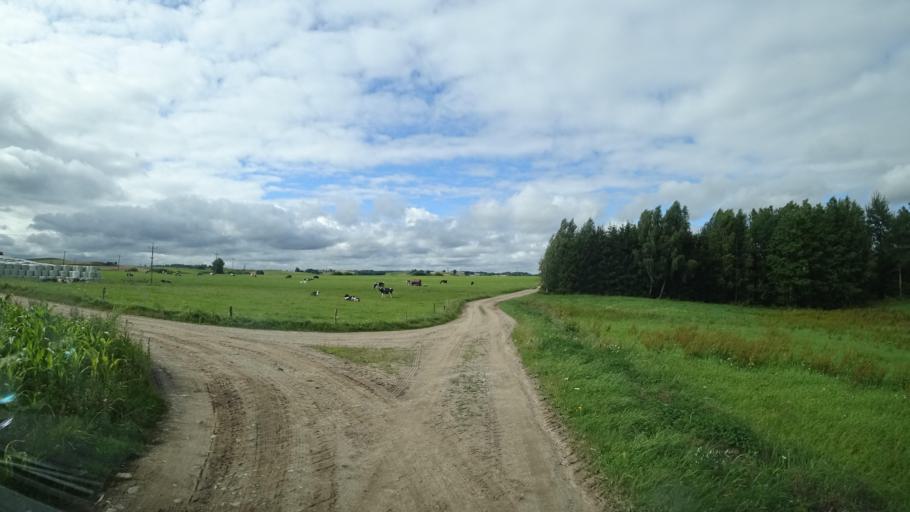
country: PL
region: Podlasie
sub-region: Suwalki
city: Suwalki
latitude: 54.3733
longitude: 22.9019
